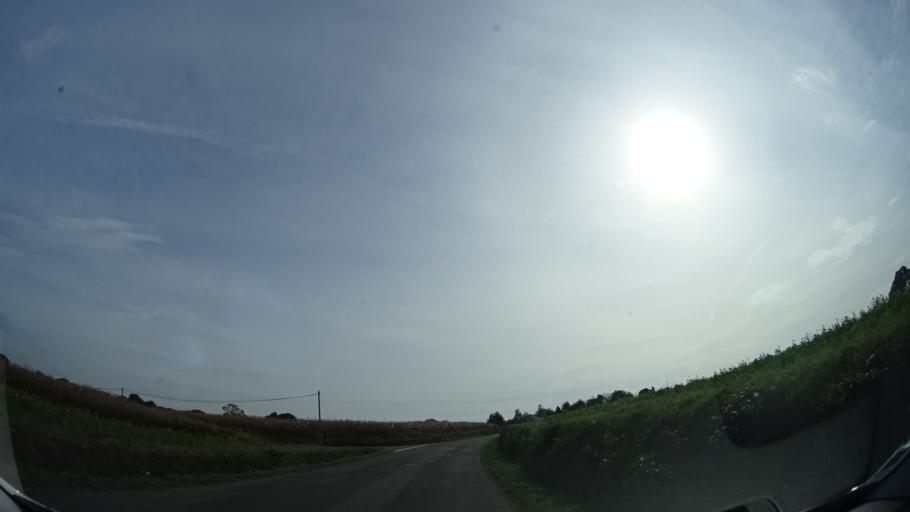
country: FR
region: Brittany
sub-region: Departement d'Ille-et-Vilaine
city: La Meziere
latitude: 48.2240
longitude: -1.7650
